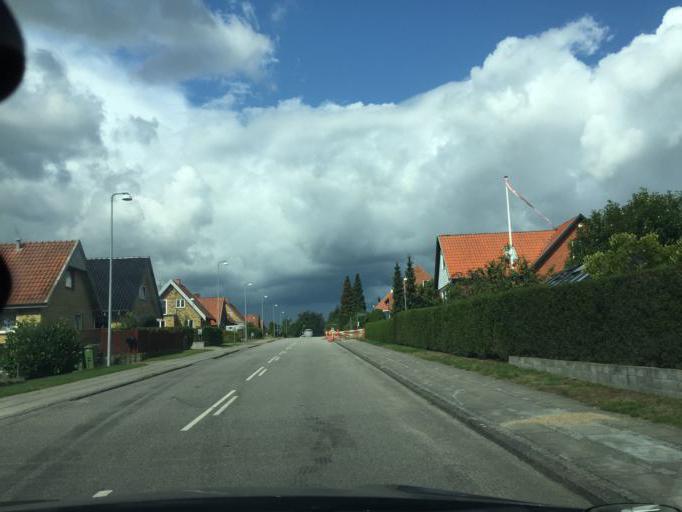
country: DK
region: South Denmark
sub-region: Odense Kommune
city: Odense
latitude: 55.4024
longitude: 10.3499
